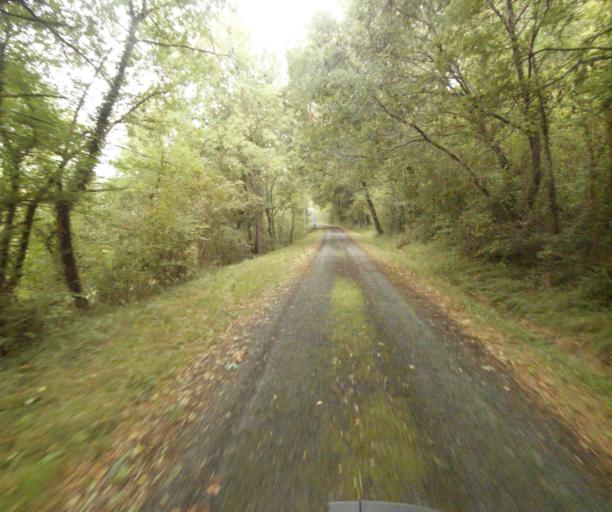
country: FR
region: Midi-Pyrenees
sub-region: Departement de la Haute-Garonne
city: Villemur-sur-Tarn
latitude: 43.8946
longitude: 1.4768
